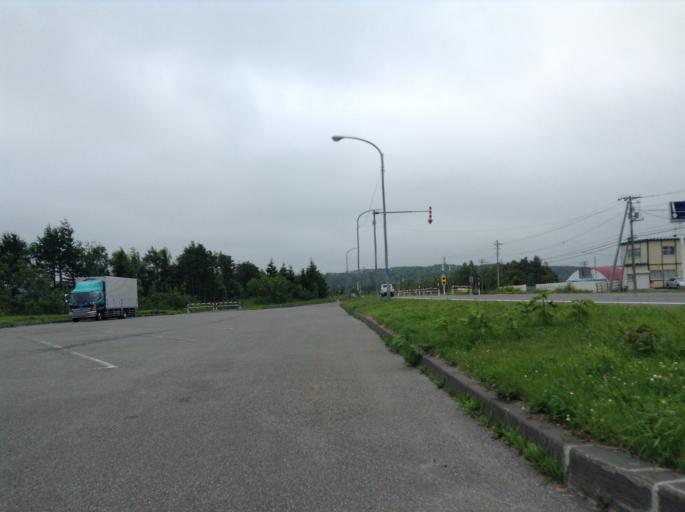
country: JP
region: Hokkaido
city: Wakkanai
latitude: 45.3641
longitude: 141.7293
